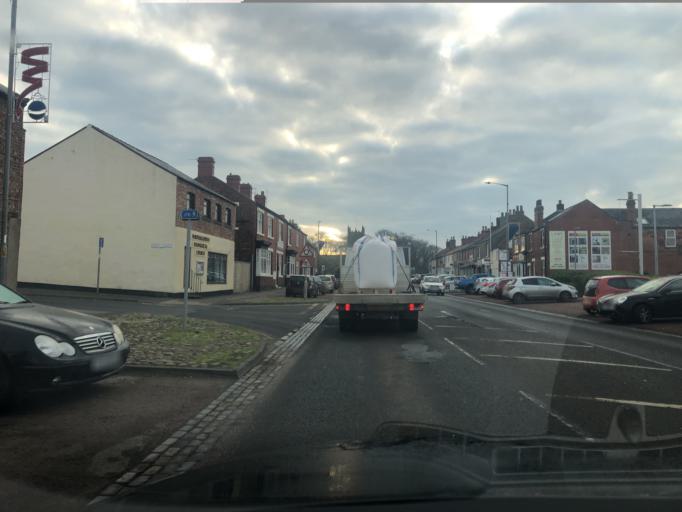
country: GB
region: England
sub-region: North Yorkshire
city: Northallerton
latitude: 54.3445
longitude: -1.4383
